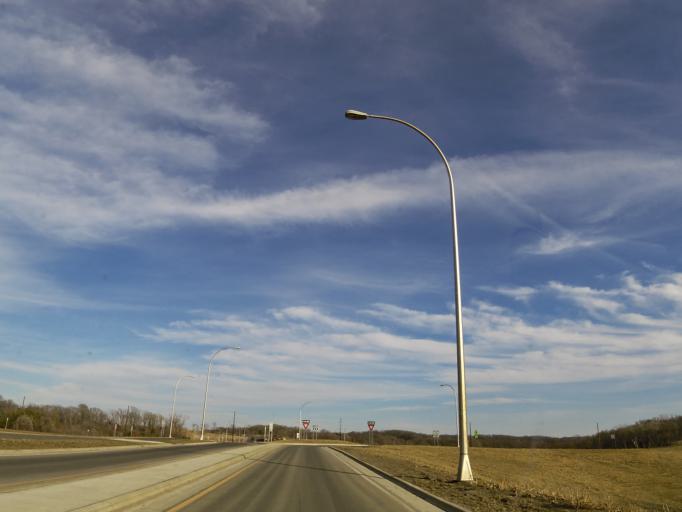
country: US
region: Minnesota
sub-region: Goodhue County
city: Cannon Falls
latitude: 44.4824
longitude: -92.9101
